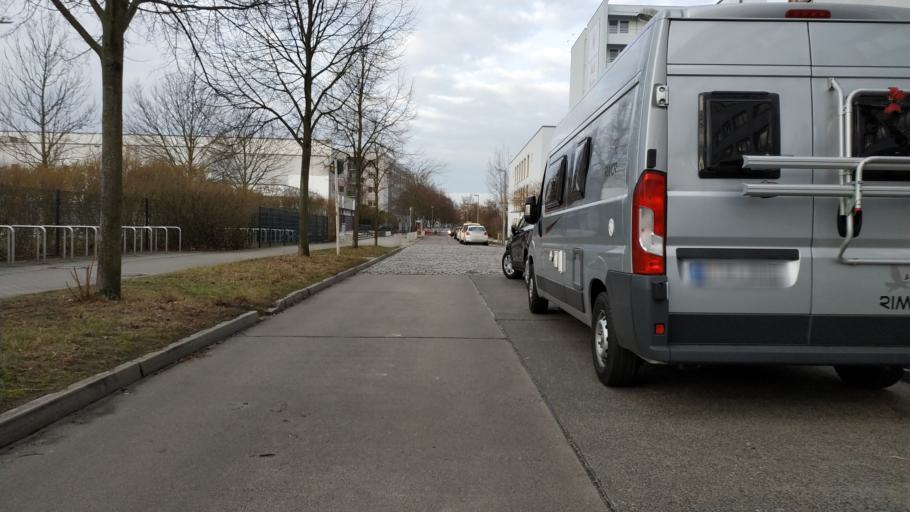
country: DE
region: Berlin
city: Hellersdorf
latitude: 52.5425
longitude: 13.5905
